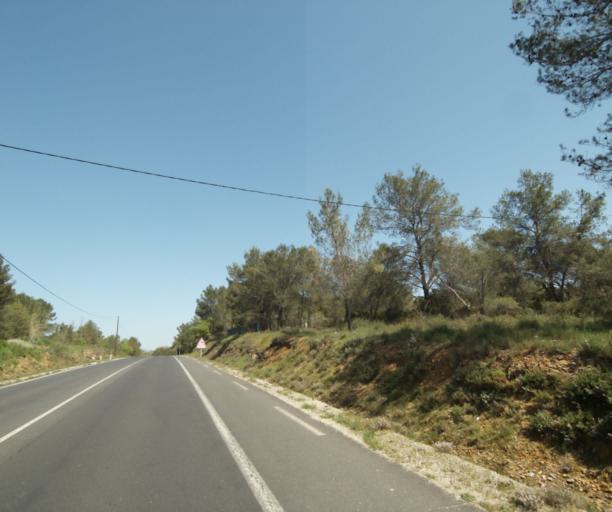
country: FR
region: Languedoc-Roussillon
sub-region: Departement de l'Herault
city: Montferrier-sur-Lez
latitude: 43.6619
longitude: 3.8663
